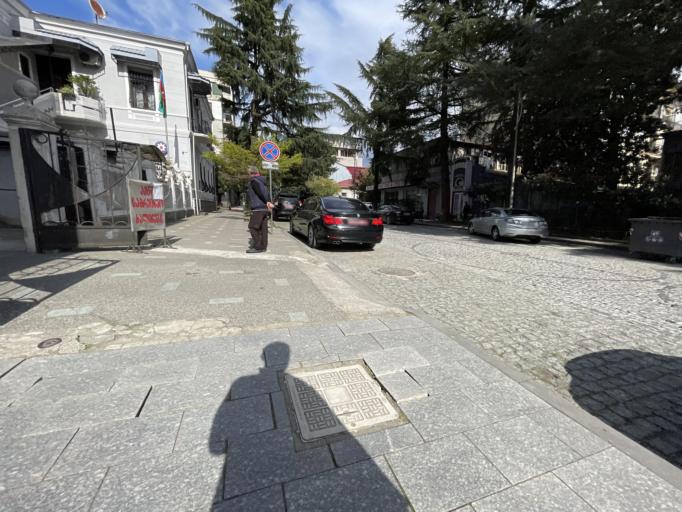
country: GE
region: Ajaria
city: Batumi
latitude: 41.6477
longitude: 41.6362
